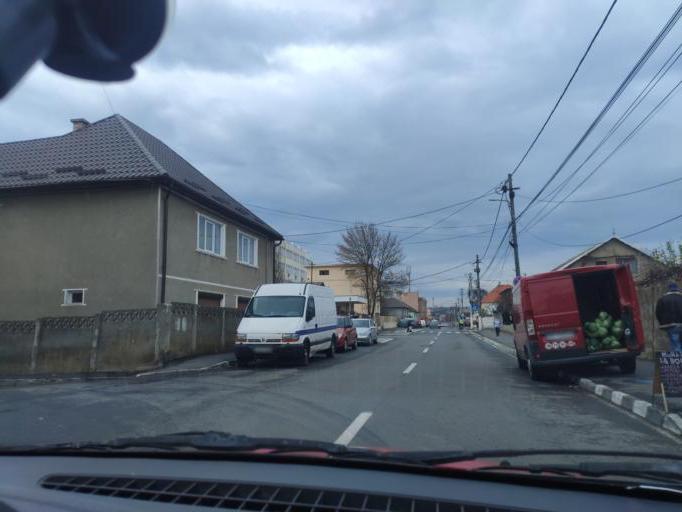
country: RO
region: Brasov
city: Codlea
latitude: 45.7035
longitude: 25.4475
